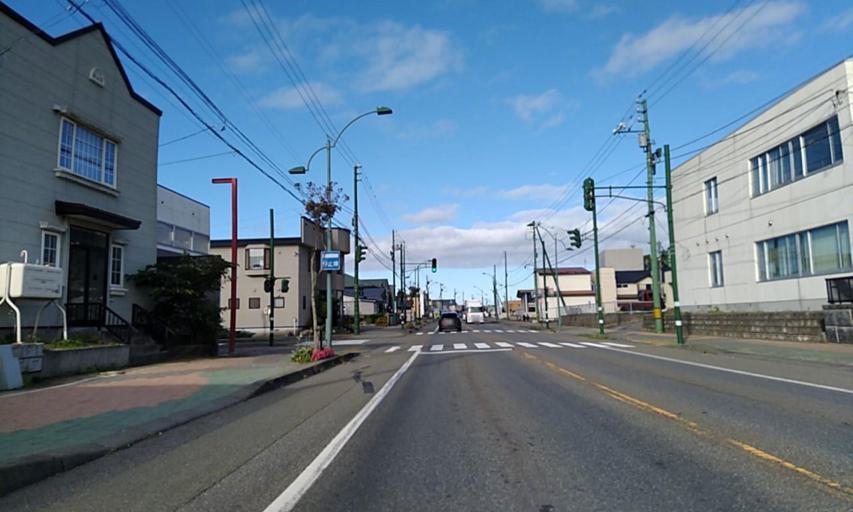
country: JP
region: Hokkaido
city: Shizunai-furukawacho
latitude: 42.2478
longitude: 142.5626
